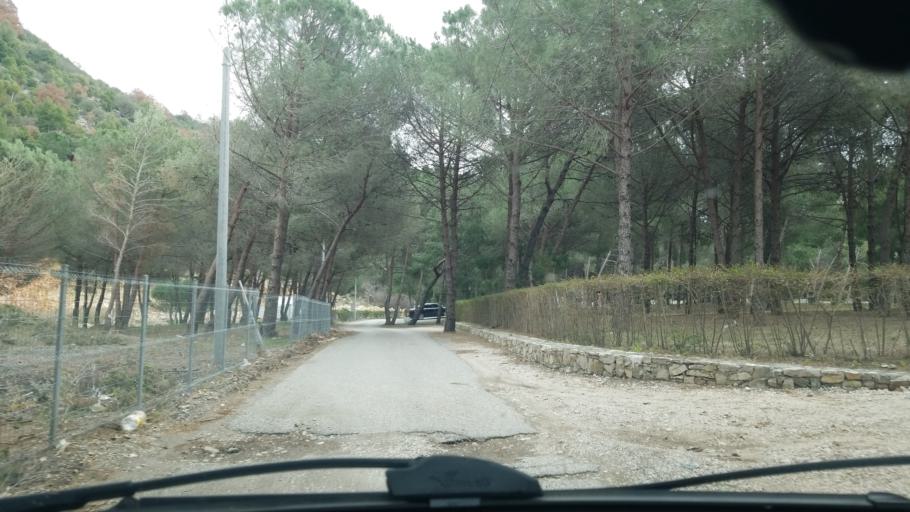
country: AL
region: Lezhe
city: Shengjin
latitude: 41.8251
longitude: 19.5579
